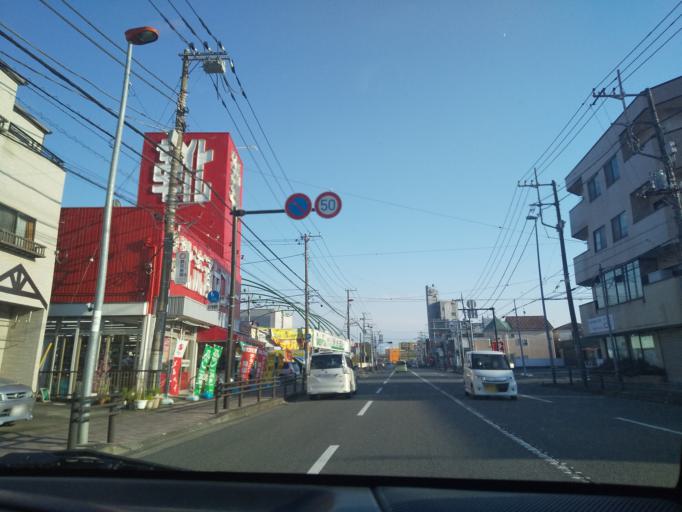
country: JP
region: Kanagawa
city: Zama
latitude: 35.5576
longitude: 139.3750
